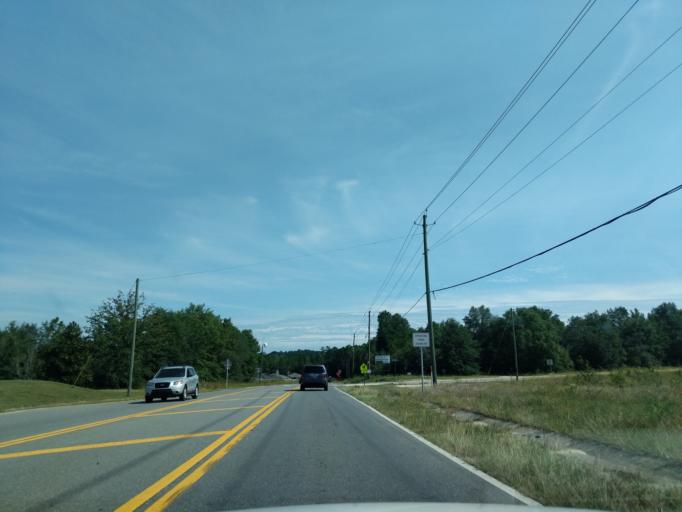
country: US
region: Florida
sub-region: Okaloosa County
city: Crestview
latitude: 30.7144
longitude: -86.6072
